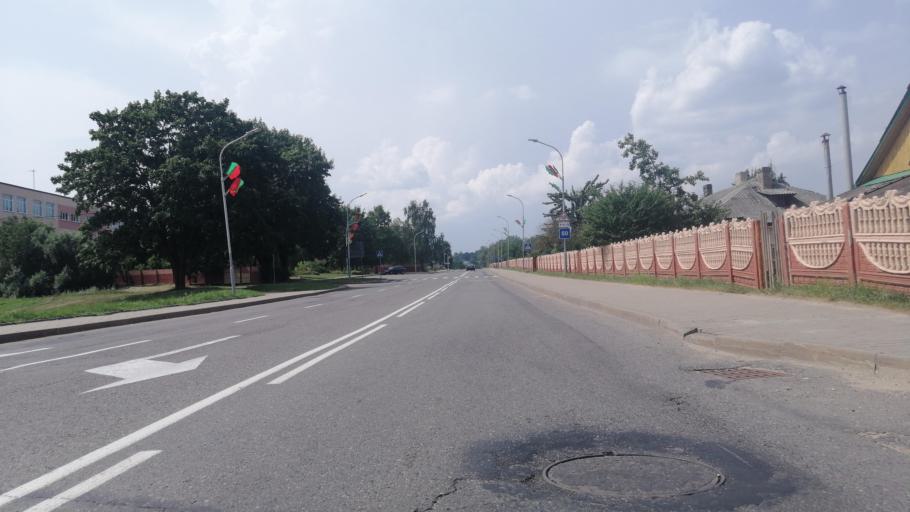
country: BY
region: Grodnenskaya
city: Navahrudak
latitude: 53.5985
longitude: 25.8439
